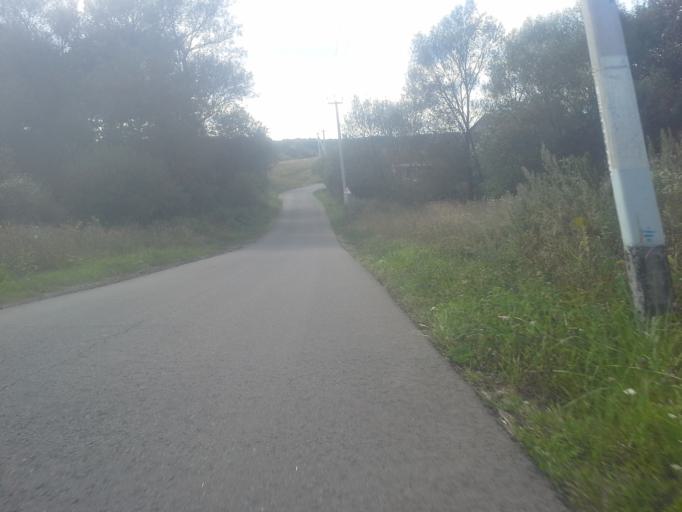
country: RU
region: Moskovskaya
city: Kievskij
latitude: 55.3155
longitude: 37.0217
